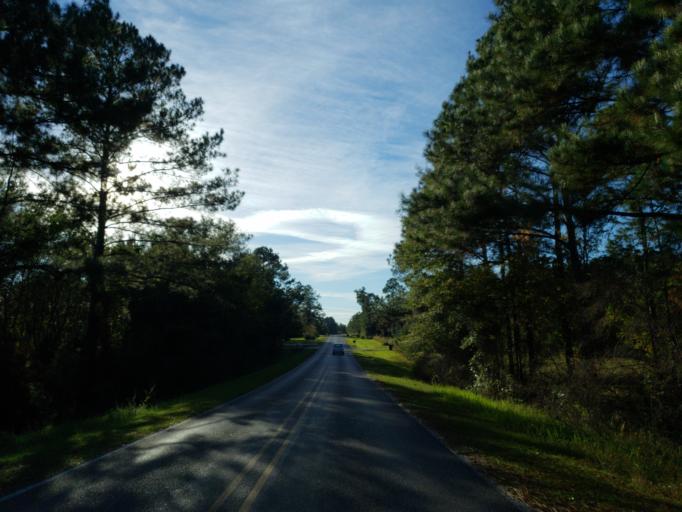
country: US
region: Mississippi
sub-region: Perry County
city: Richton
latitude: 31.3383
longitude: -88.8006
